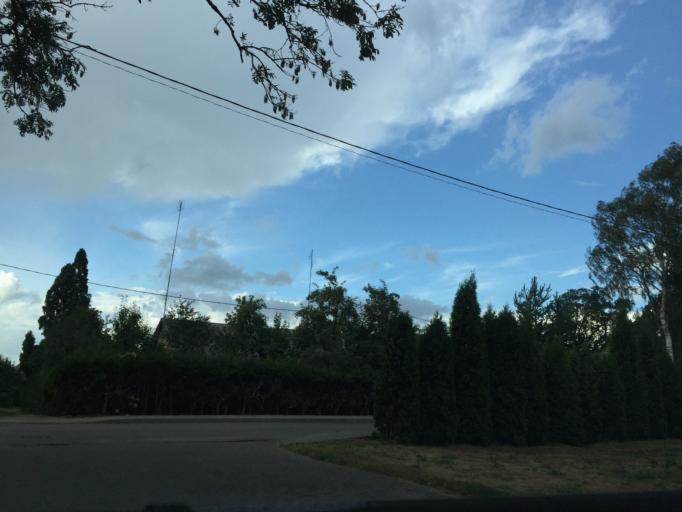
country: LT
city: Zagare
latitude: 56.3076
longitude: 23.3873
